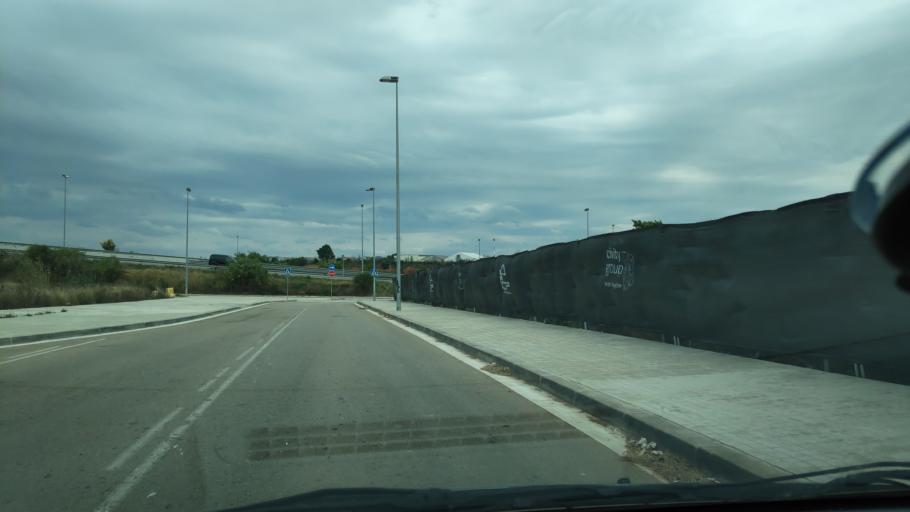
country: ES
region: Catalonia
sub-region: Provincia de Barcelona
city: Barbera del Valles
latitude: 41.5139
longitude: 2.1048
